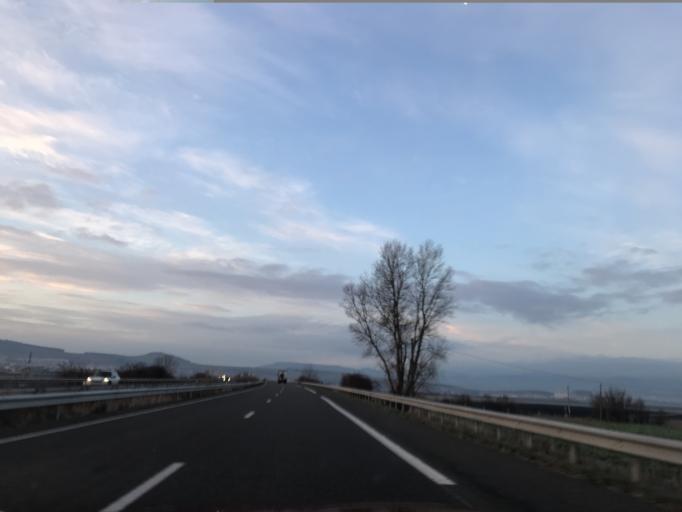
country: FR
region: Auvergne
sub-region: Departement du Puy-de-Dome
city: Malintrat
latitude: 45.7963
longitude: 3.2073
